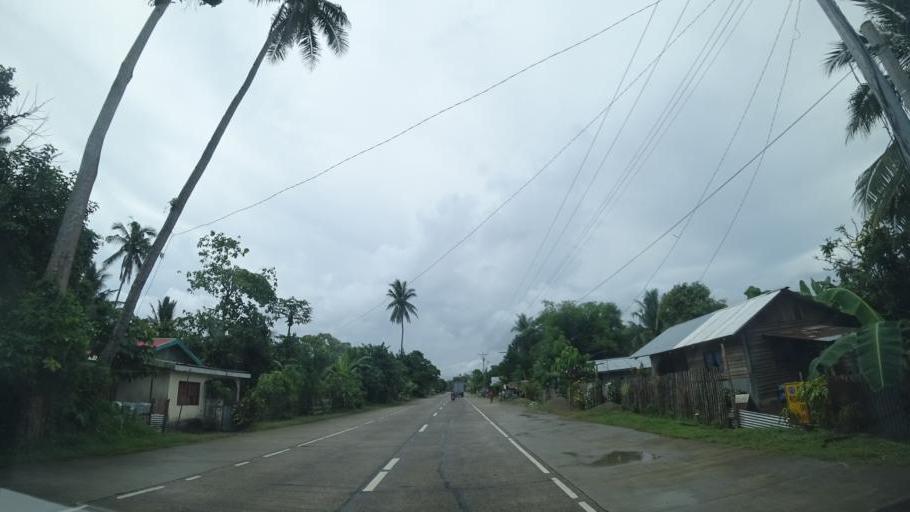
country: PH
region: Eastern Visayas
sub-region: Province of Leyte
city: Liberty
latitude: 10.8609
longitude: 124.9945
